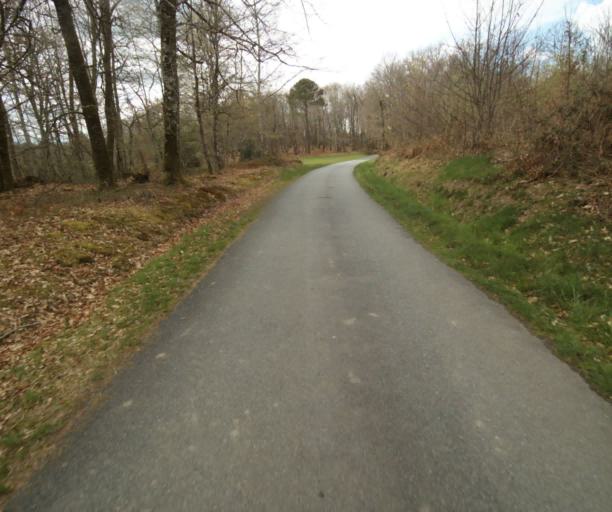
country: FR
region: Limousin
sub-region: Departement de la Correze
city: Argentat
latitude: 45.1923
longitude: 1.9244
